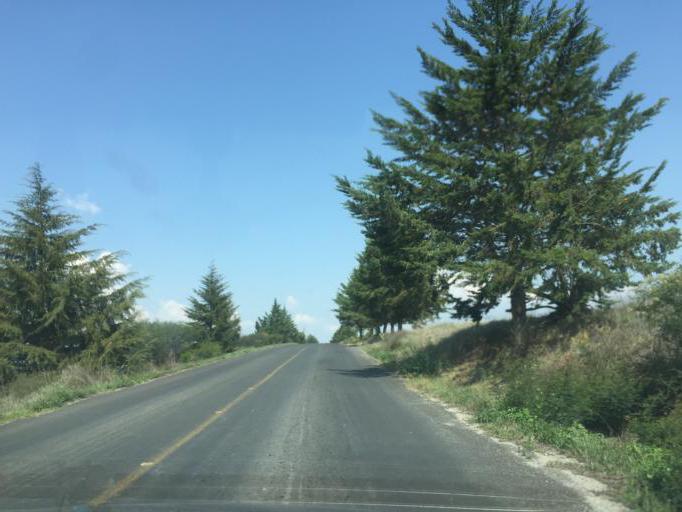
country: MX
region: Hidalgo
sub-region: Cardonal
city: Pozuelos
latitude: 20.6157
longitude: -99.0626
